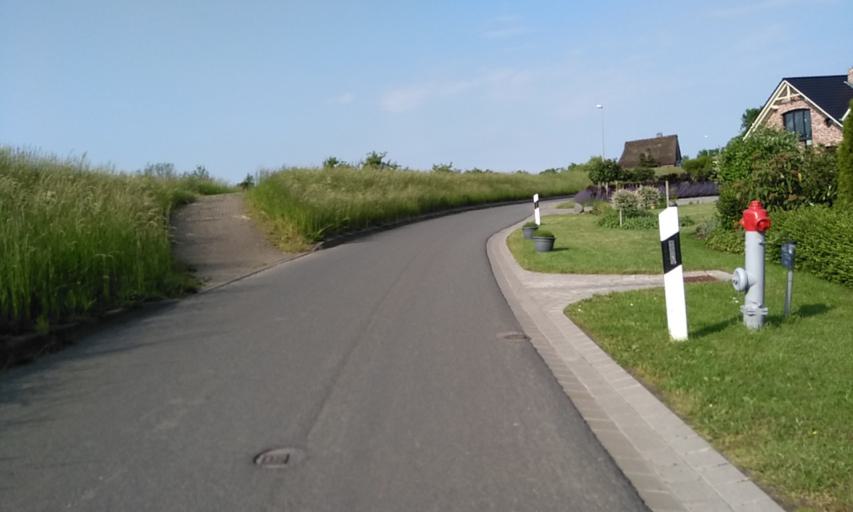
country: DE
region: Lower Saxony
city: Buxtehude
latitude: 53.4970
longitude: 9.7218
